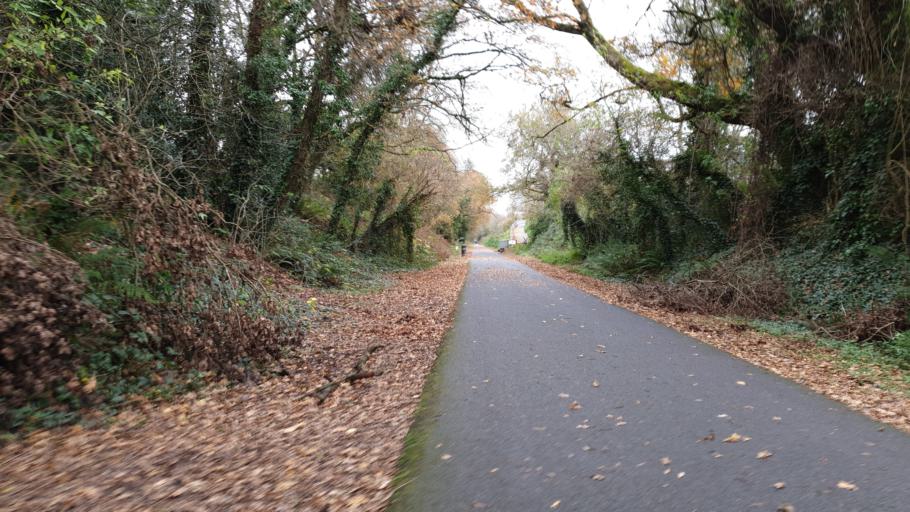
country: IE
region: Munster
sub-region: County Cork
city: Passage West
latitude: 51.8843
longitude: -8.4052
